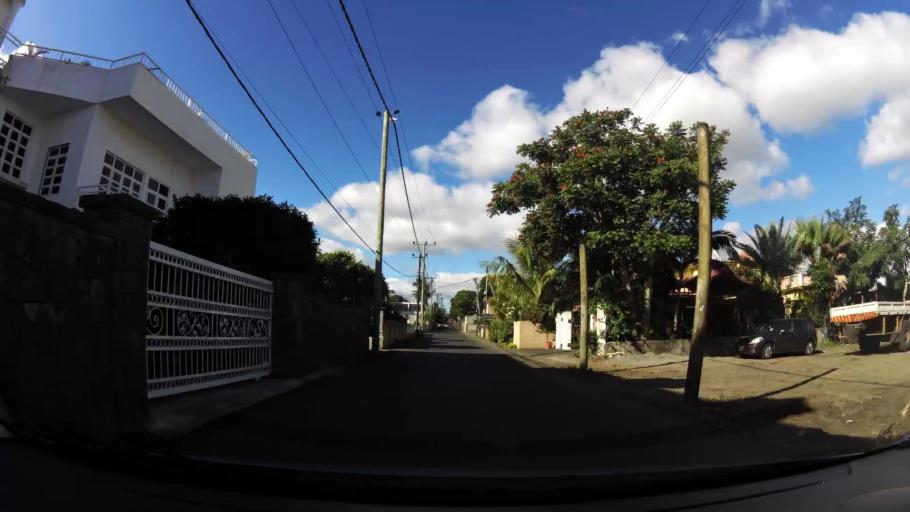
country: MU
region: Plaines Wilhems
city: Vacoas
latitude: -20.2850
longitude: 57.4862
